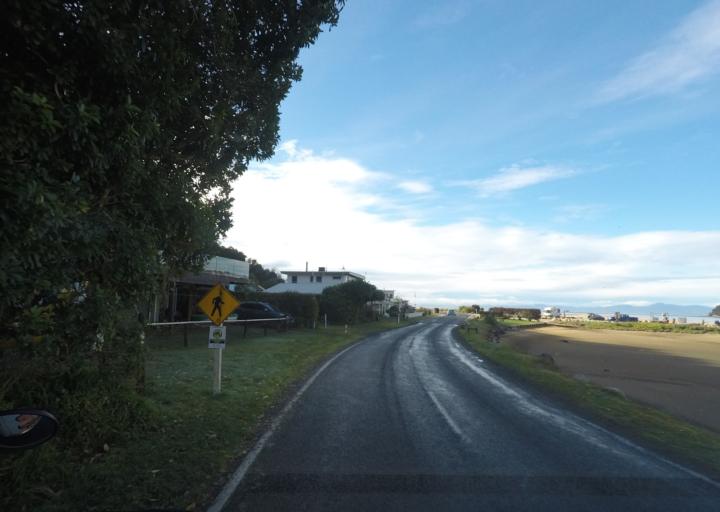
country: NZ
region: Tasman
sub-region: Tasman District
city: Motueka
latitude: -41.0089
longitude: 173.0067
